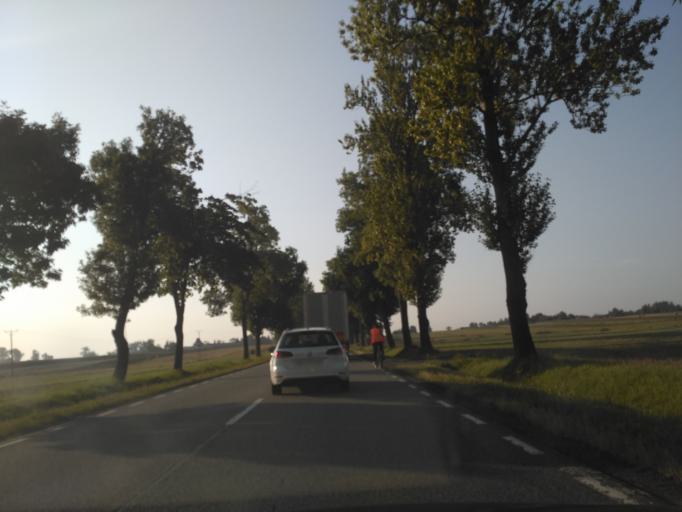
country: PL
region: Lublin Voivodeship
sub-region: Powiat krasnicki
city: Szastarka
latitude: 50.8385
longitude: 22.3008
